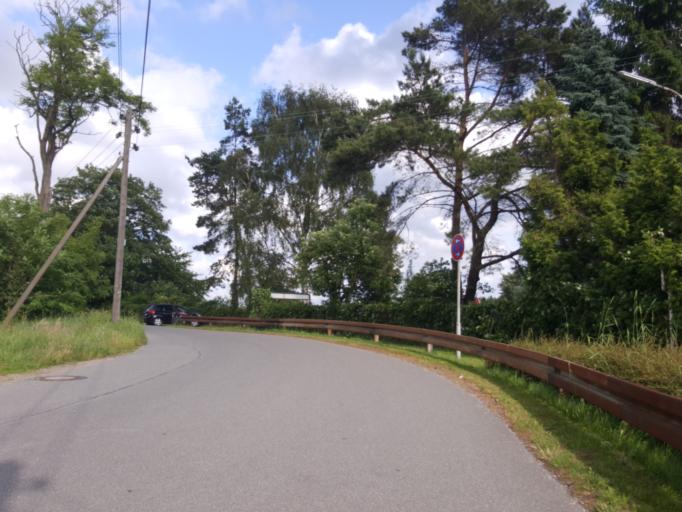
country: DE
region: Hamburg
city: Marienthal
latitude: 53.5403
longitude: 10.0821
